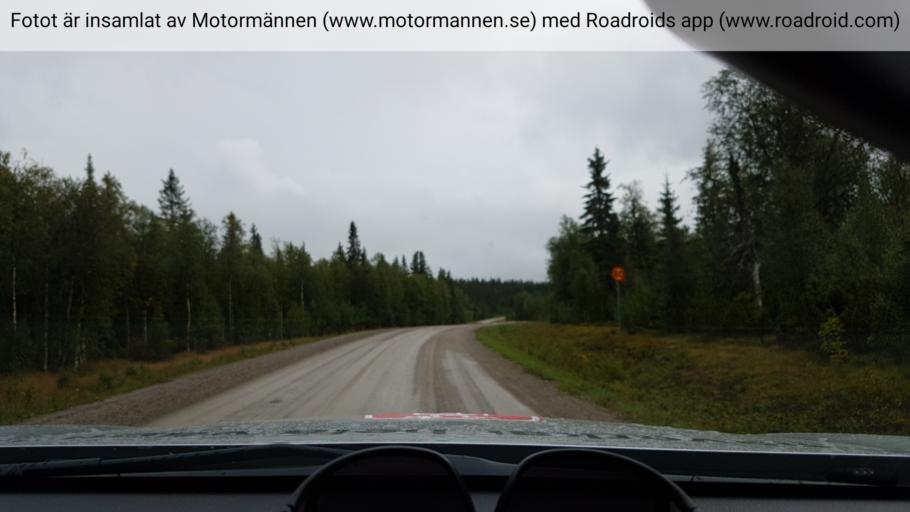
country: SE
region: Vaesterbotten
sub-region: Storumans Kommun
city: Storuman
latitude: 64.9288
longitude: 17.2467
